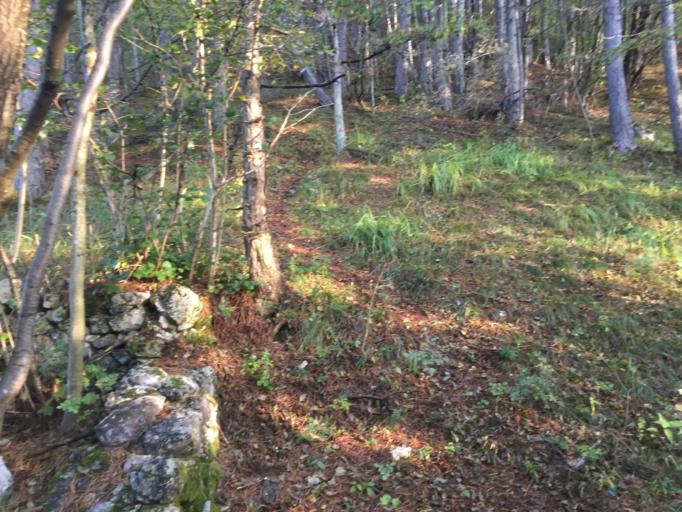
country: IT
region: Friuli Venezia Giulia
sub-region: Provincia di Udine
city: Chiusaforte
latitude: 46.4024
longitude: 13.3307
